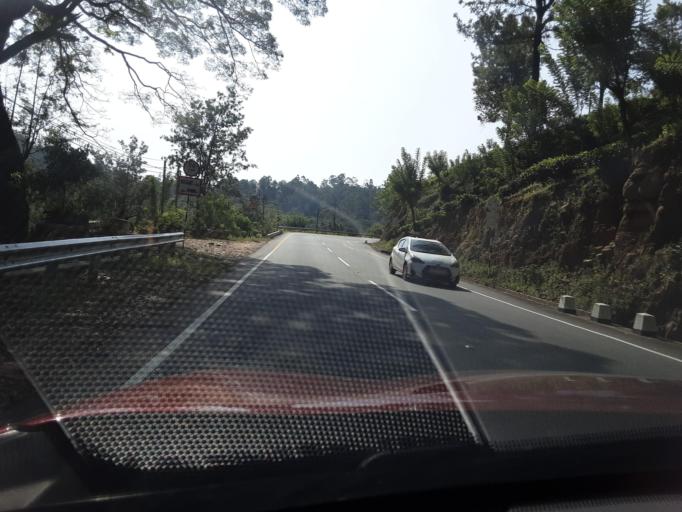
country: LK
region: Uva
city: Badulla
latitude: 6.9596
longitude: 81.1151
